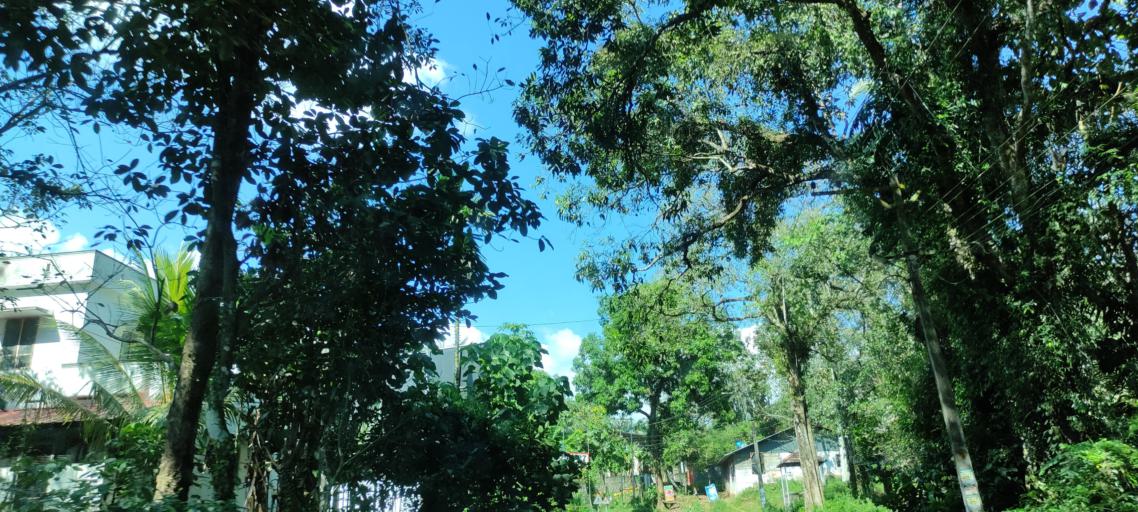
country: IN
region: Kerala
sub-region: Pattanamtitta
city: Adur
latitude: 9.1929
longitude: 76.7455
